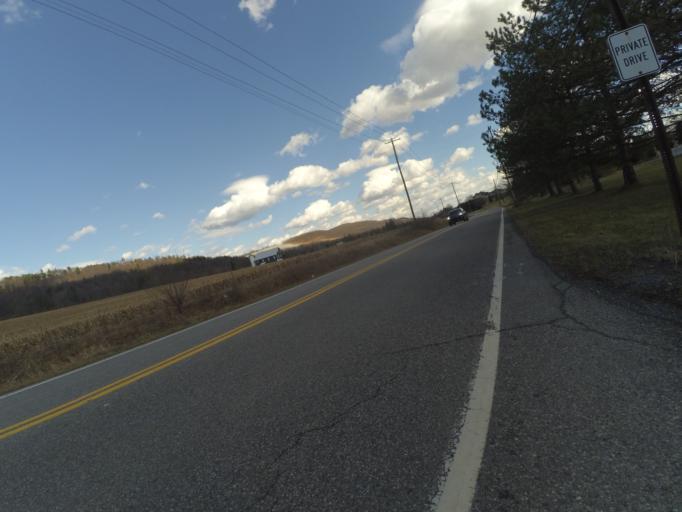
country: US
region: Pennsylvania
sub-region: Centre County
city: Stormstown
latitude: 40.8213
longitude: -77.9719
